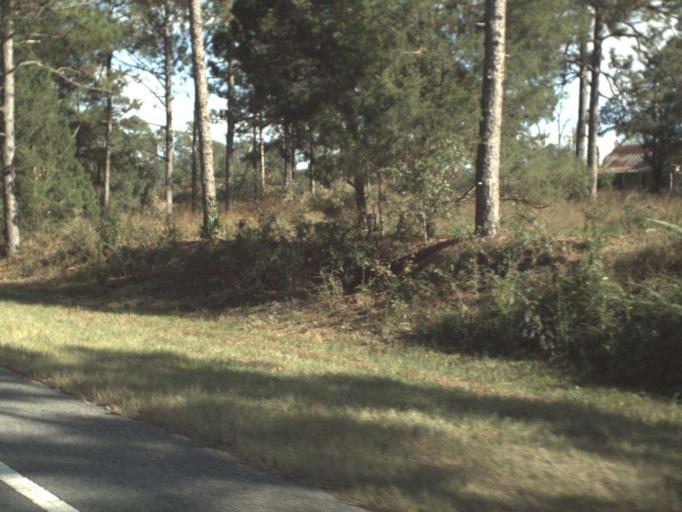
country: US
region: Florida
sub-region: Washington County
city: Chipley
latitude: 30.7820
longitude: -85.5104
